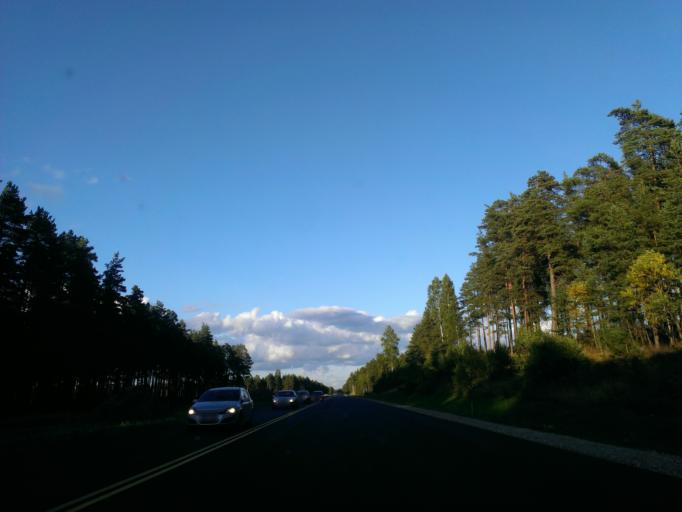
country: LV
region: Garkalne
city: Garkalne
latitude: 57.0285
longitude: 24.3659
